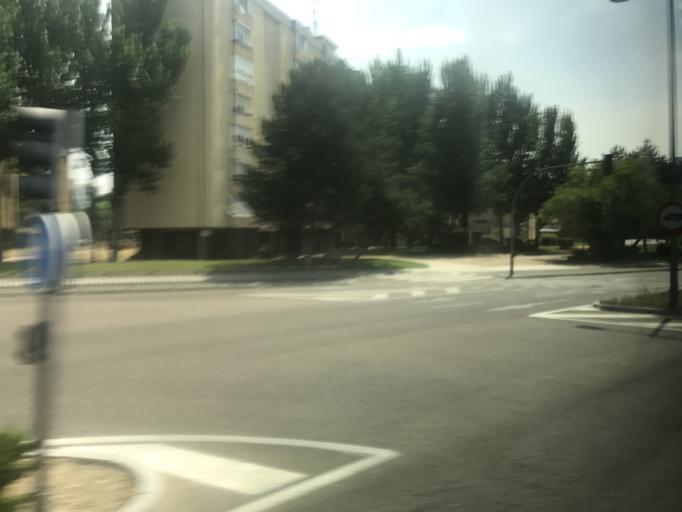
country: ES
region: Castille and Leon
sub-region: Provincia de Valladolid
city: Valladolid
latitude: 41.6481
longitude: -4.7409
